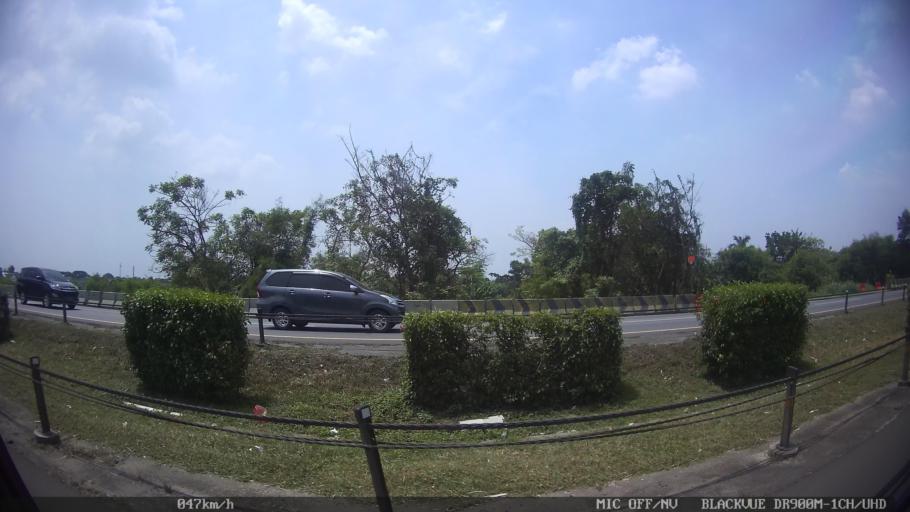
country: ID
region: Banten
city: Serang
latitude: -6.1294
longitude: 106.1969
